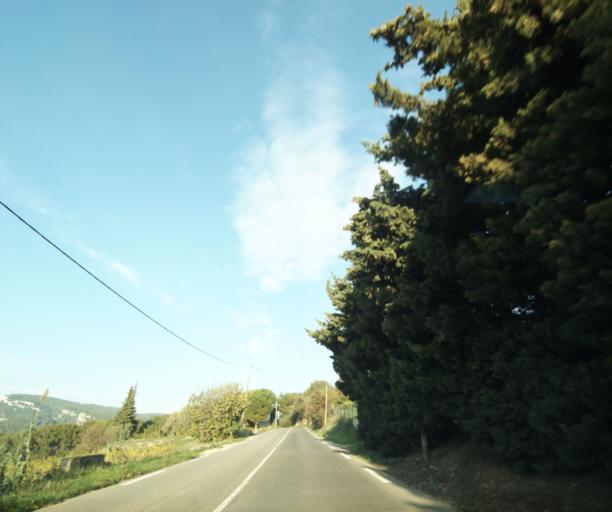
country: FR
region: Provence-Alpes-Cote d'Azur
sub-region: Departement des Bouches-du-Rhone
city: Cassis
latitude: 43.2160
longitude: 5.5568
